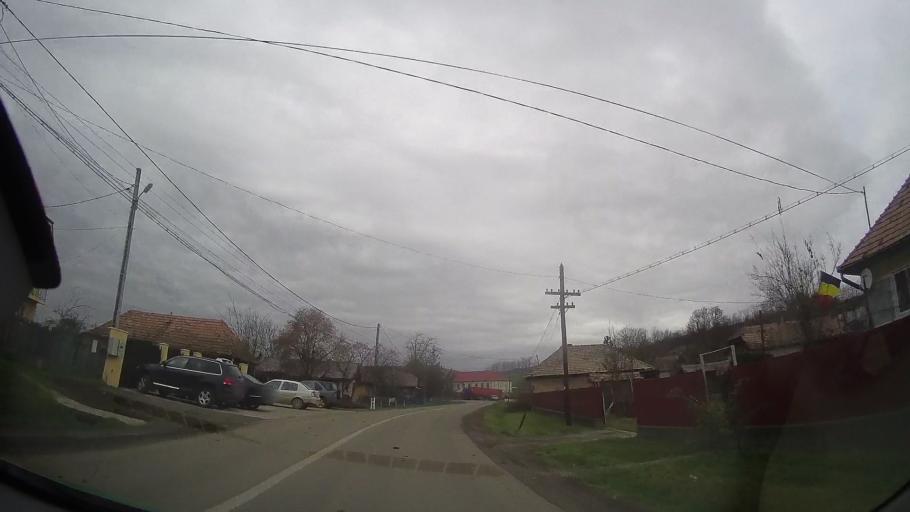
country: RO
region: Mures
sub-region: Comuna Craesti
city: Craiesti
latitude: 46.7577
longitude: 24.4250
